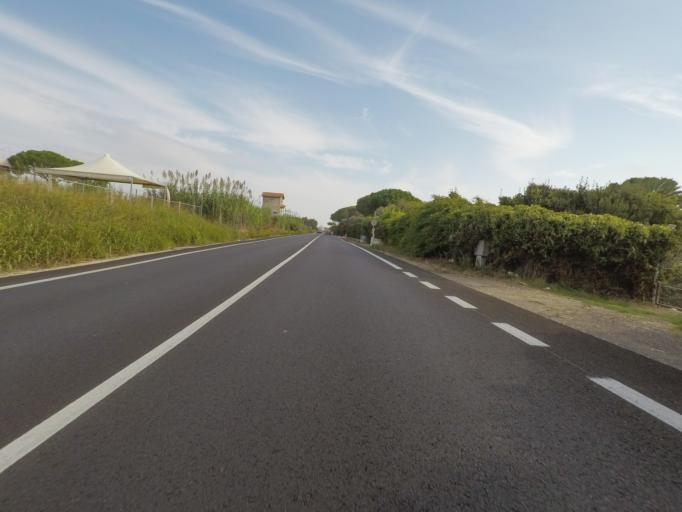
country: IT
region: Latium
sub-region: Citta metropolitana di Roma Capitale
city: Santa Marinella
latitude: 42.0480
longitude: 11.8216
